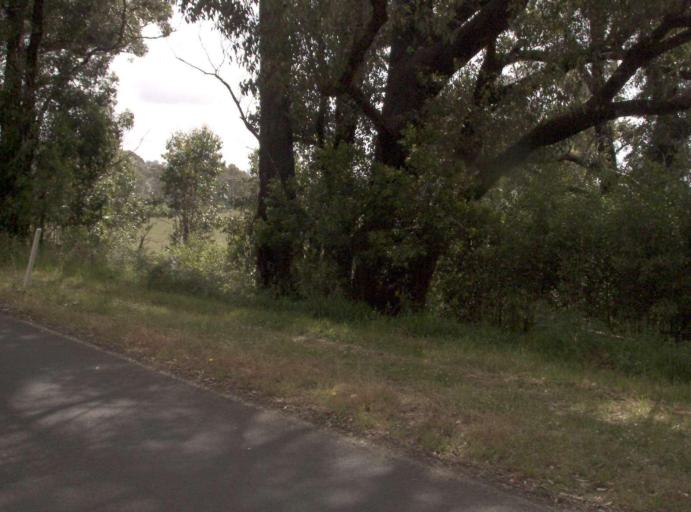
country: AU
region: Victoria
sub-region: Latrobe
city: Traralgon
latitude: -38.3413
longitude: 146.5723
